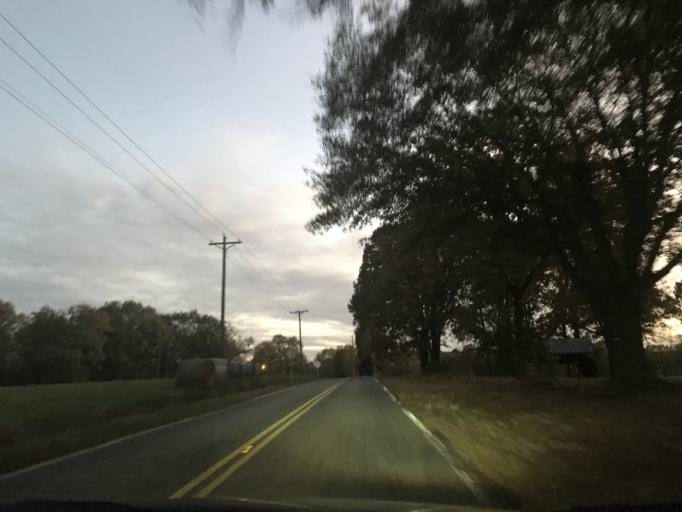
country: US
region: South Carolina
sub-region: Spartanburg County
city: Mayo
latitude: 35.0698
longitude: -81.8999
